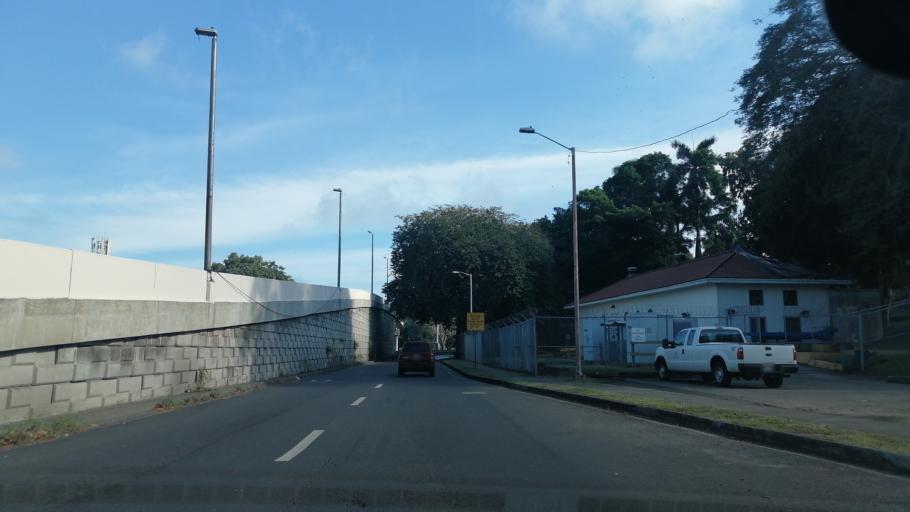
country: PA
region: Panama
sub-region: Distrito de Panama
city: Ancon
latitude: 8.9614
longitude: -79.5550
